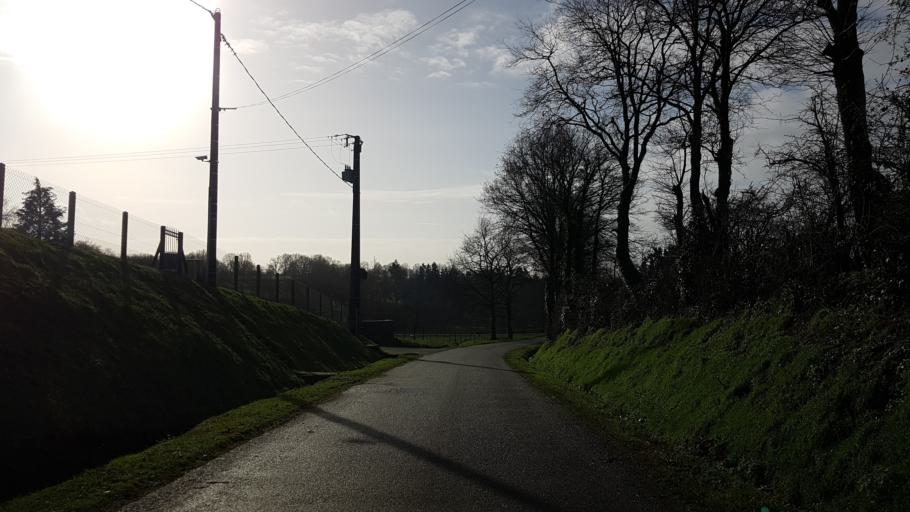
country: FR
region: Poitou-Charentes
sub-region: Departement de la Charente
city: Etagnac
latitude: 45.8923
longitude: 0.7752
